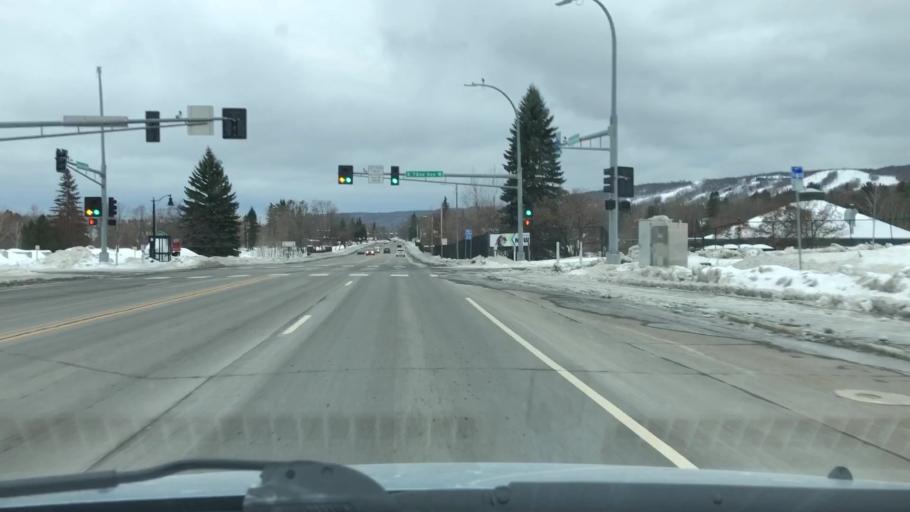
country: US
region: Minnesota
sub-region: Saint Louis County
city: Proctor
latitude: 46.7257
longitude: -92.1880
